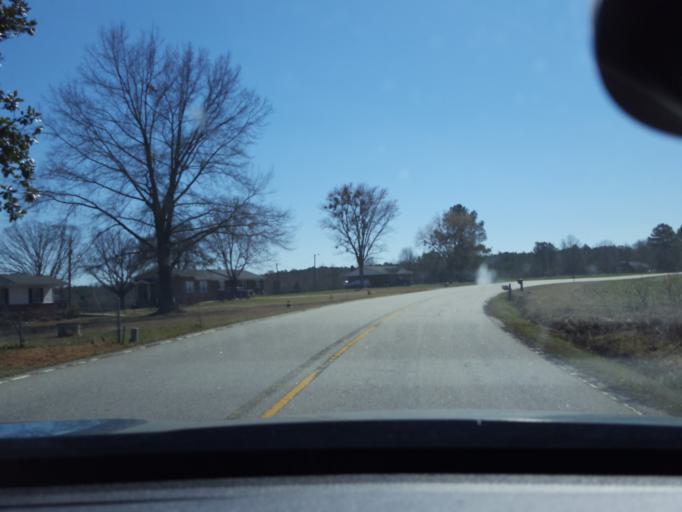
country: US
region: North Carolina
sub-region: Halifax County
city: South Rosemary
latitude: 36.3911
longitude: -77.8991
